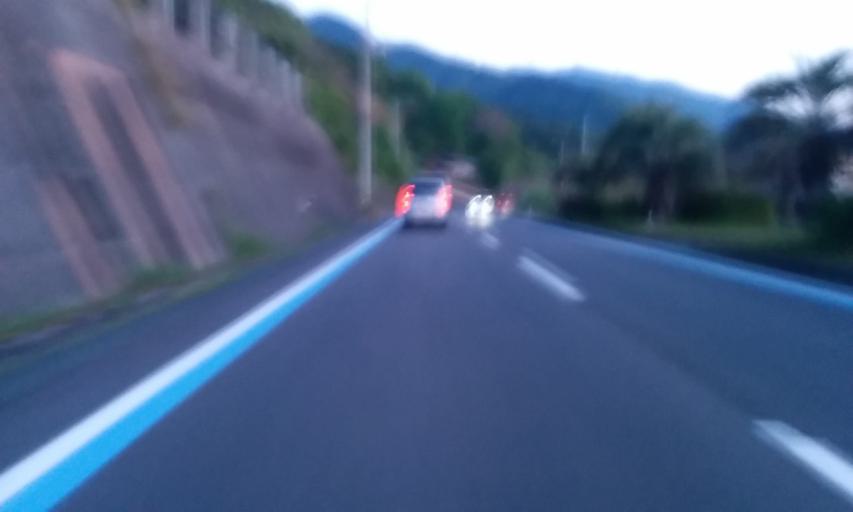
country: JP
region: Ehime
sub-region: Nishiuwa-gun
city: Ikata-cho
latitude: 33.5532
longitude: 132.4267
